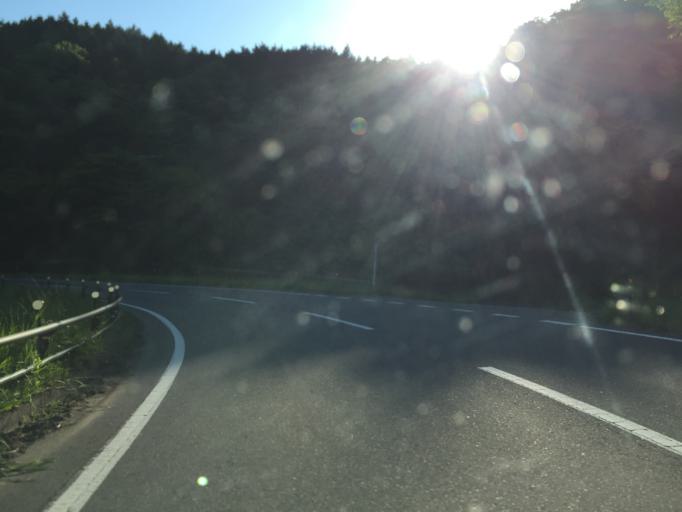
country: JP
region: Ibaraki
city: Daigo
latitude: 36.9210
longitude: 140.5165
